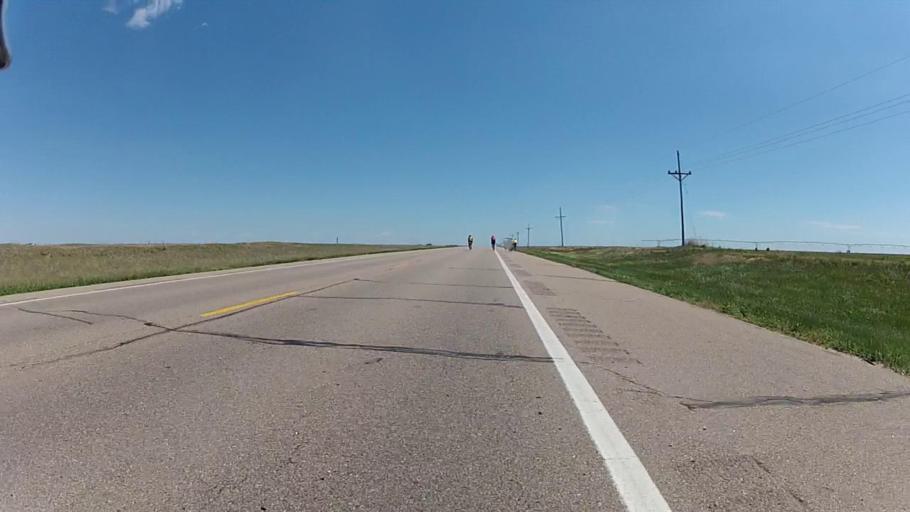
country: US
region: Kansas
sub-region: Ford County
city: Dodge City
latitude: 37.6775
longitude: -100.1870
